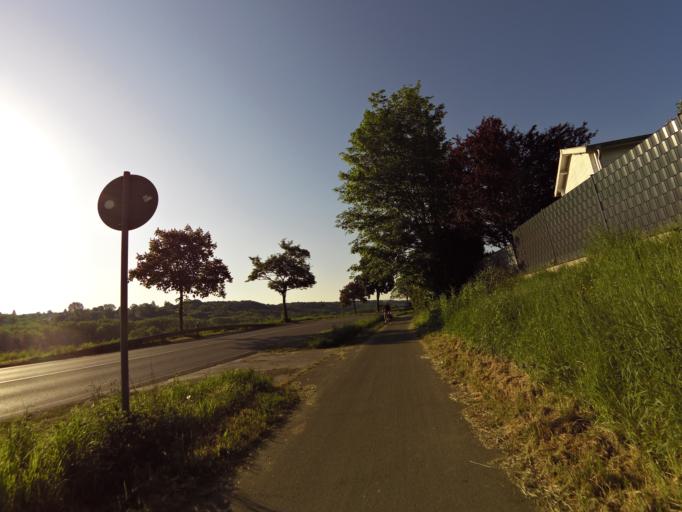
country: DE
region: North Rhine-Westphalia
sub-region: Regierungsbezirk Koln
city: Bonn
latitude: 50.6969
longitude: 7.0705
